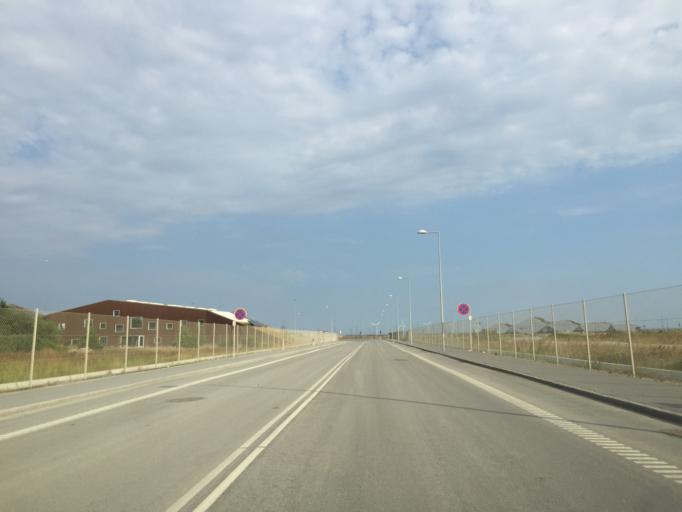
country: DK
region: Capital Region
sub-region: Gentofte Kommune
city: Charlottenlund
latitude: 55.7182
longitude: 12.6168
